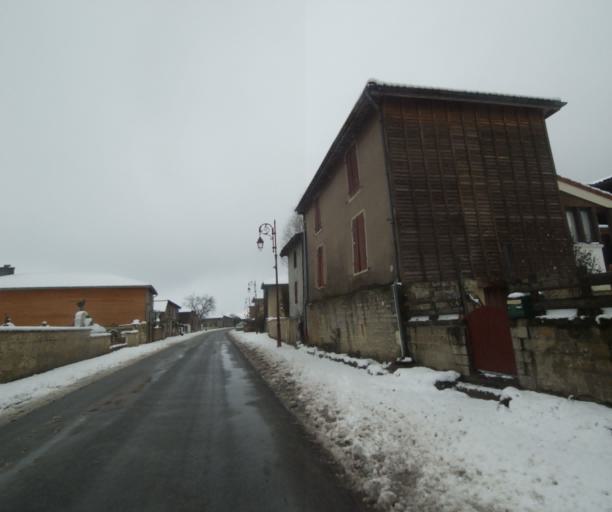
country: FR
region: Champagne-Ardenne
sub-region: Departement de la Haute-Marne
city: Laneuville-a-Remy
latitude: 48.4614
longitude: 4.8471
